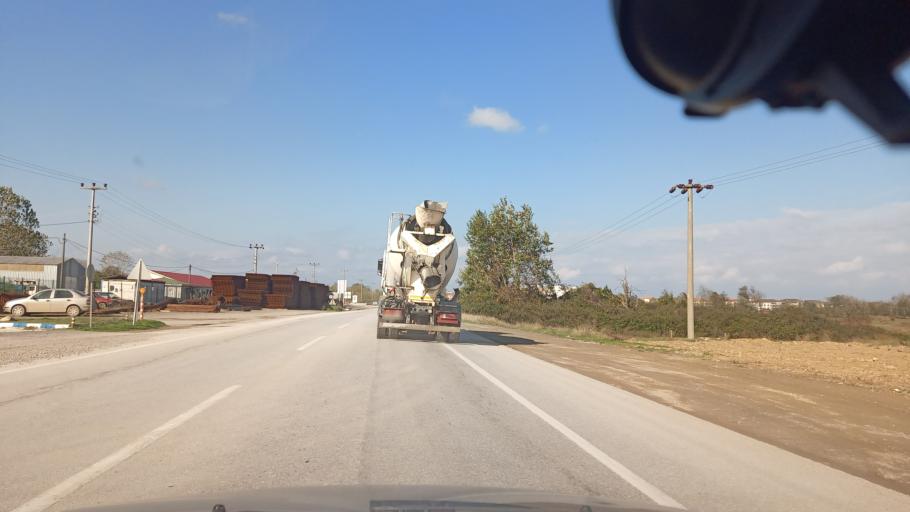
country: TR
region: Sakarya
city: Karasu
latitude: 41.1135
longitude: 30.6587
